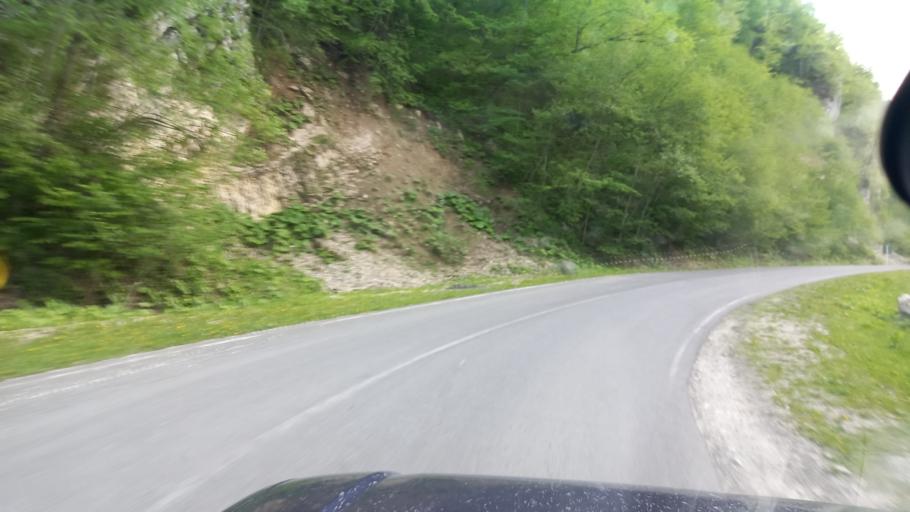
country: RU
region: North Ossetia
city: Tarskoye
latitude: 42.8936
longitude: 44.9450
